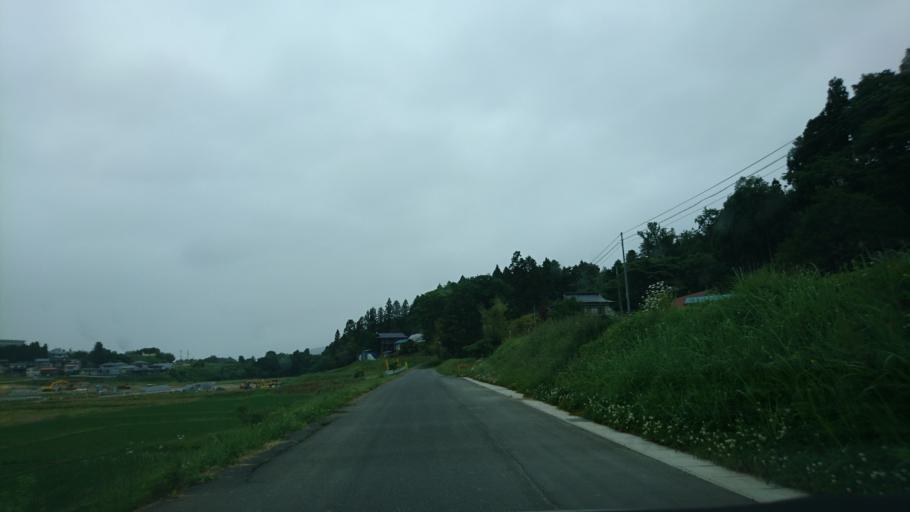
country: JP
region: Iwate
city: Ichinoseki
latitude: 38.9306
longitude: 141.1752
